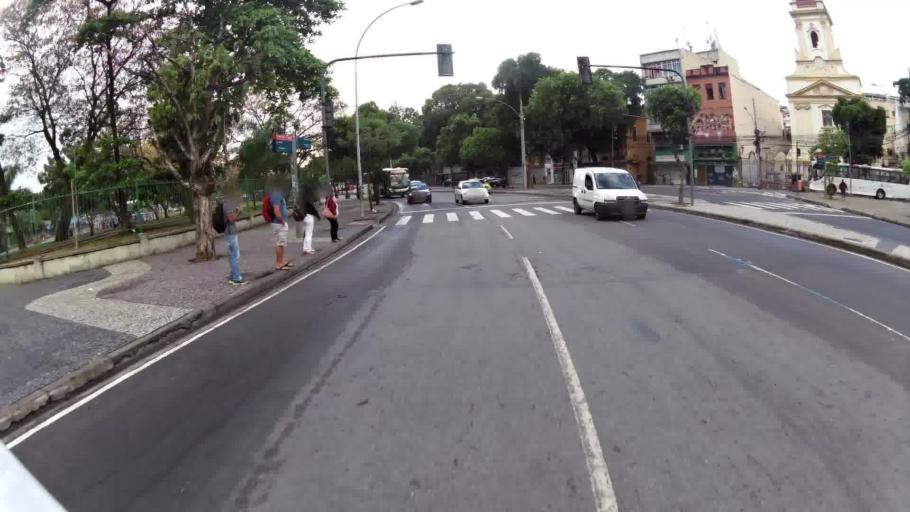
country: BR
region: Rio de Janeiro
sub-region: Rio De Janeiro
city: Rio de Janeiro
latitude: -22.9145
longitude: -43.2071
